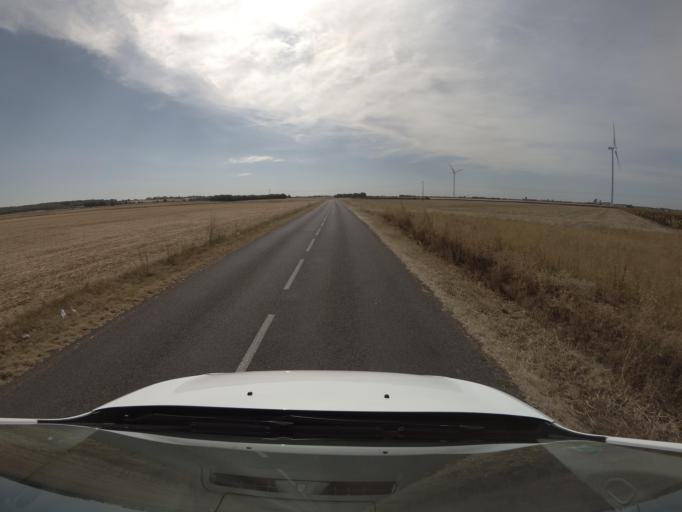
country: FR
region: Poitou-Charentes
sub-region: Departement des Deux-Sevres
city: Saint-Leger-de-Montbrun
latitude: 46.9872
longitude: -0.1634
